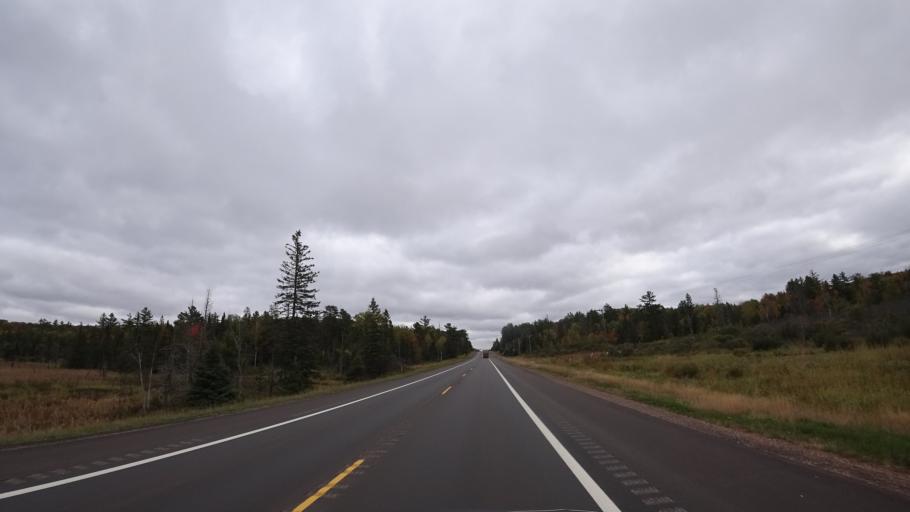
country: US
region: Michigan
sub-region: Marquette County
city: West Ishpeming
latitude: 46.4958
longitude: -87.8789
